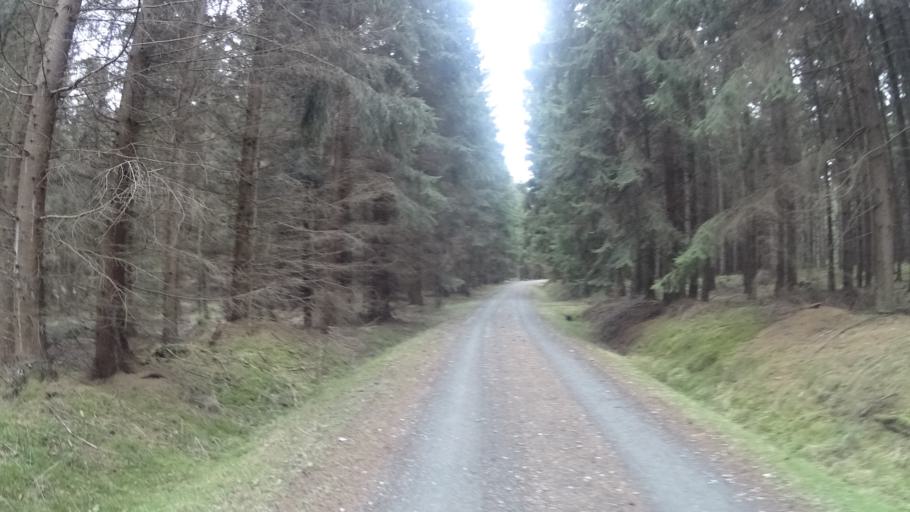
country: DE
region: Saxony
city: Pausa
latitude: 50.6156
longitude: 12.0038
